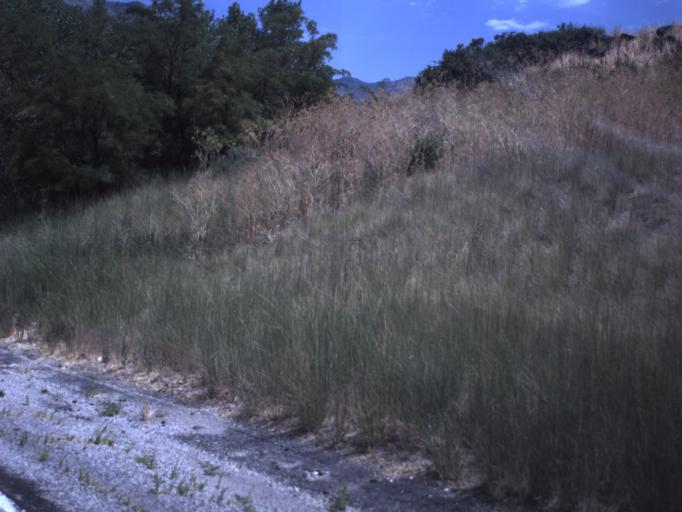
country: US
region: Utah
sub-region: Box Elder County
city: Elwood
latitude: 41.7126
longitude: -112.1228
